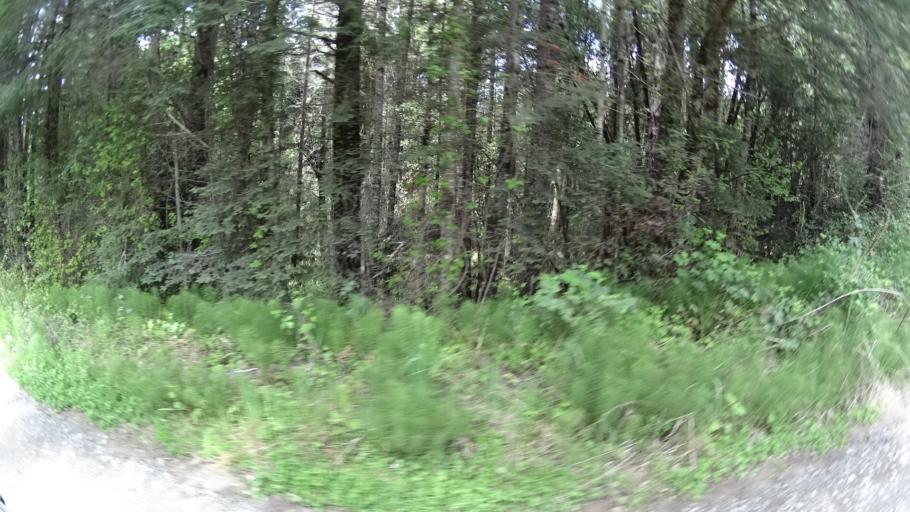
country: US
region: California
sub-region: Humboldt County
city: Blue Lake
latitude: 40.7953
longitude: -123.8754
